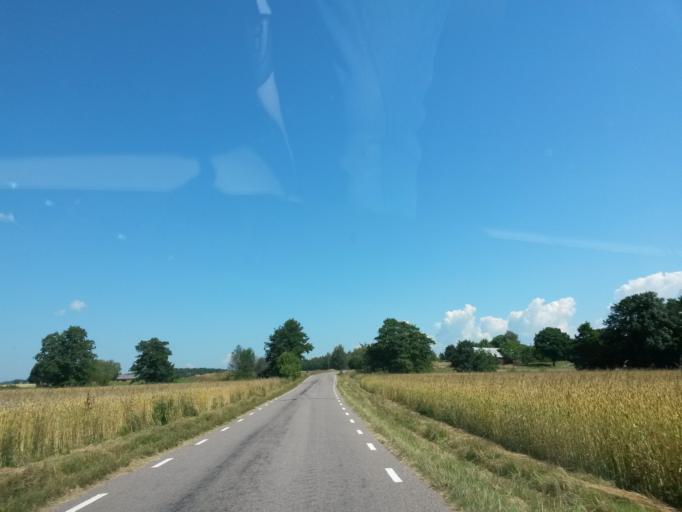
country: SE
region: Vaestra Goetaland
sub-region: Grastorps Kommun
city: Graestorp
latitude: 58.3435
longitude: 12.7637
